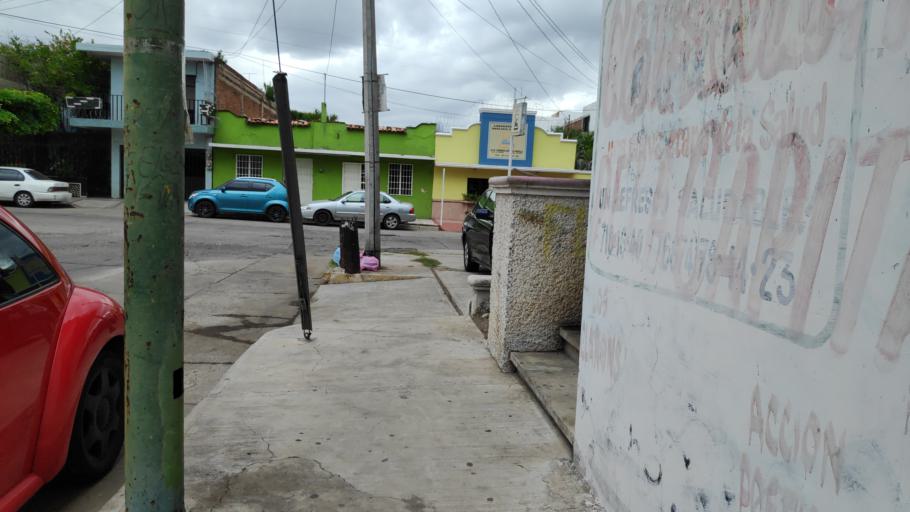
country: MX
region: Sinaloa
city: Culiacan
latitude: 24.8068
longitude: -107.3890
